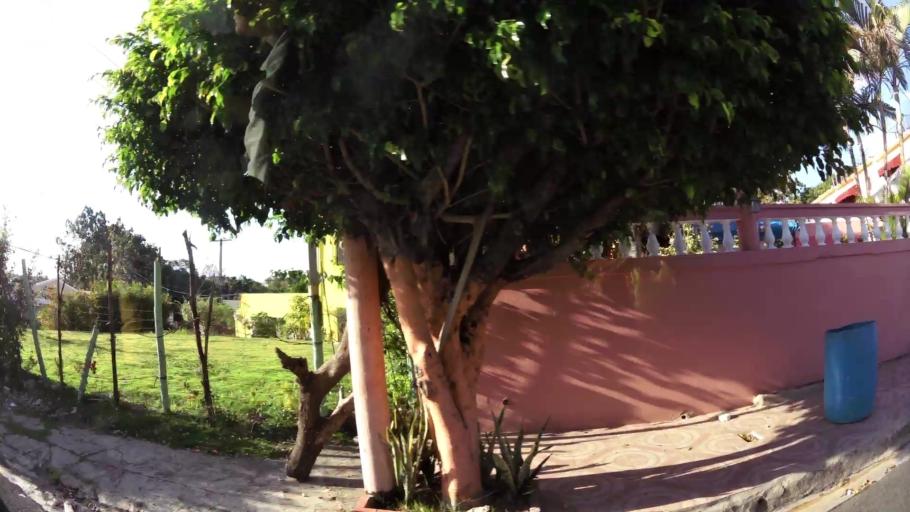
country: DO
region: Nacional
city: Santo Domingo
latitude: 18.4964
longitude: -69.9703
